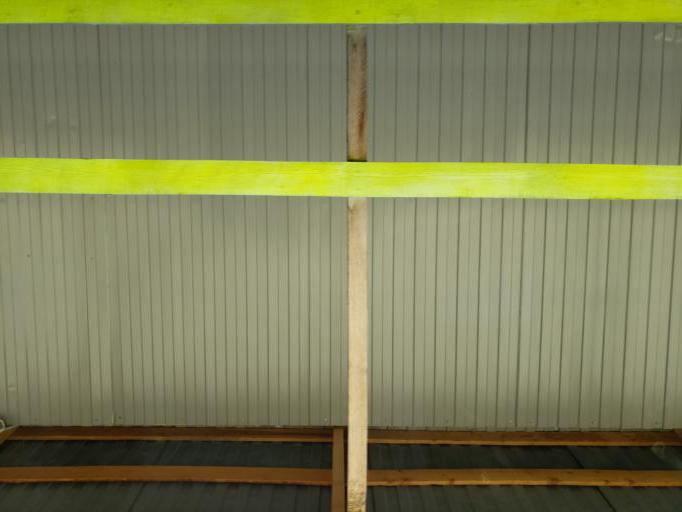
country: RU
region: St.-Petersburg
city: Saint Petersburg
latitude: 59.9434
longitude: 30.3271
